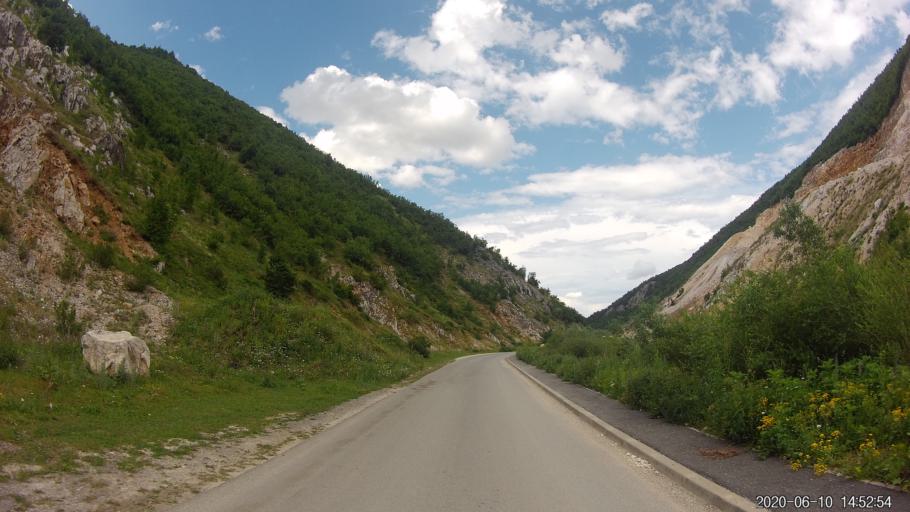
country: XK
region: Ferizaj
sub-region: Komuna e Shtimes
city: Shtime
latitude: 42.4018
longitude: 20.9835
